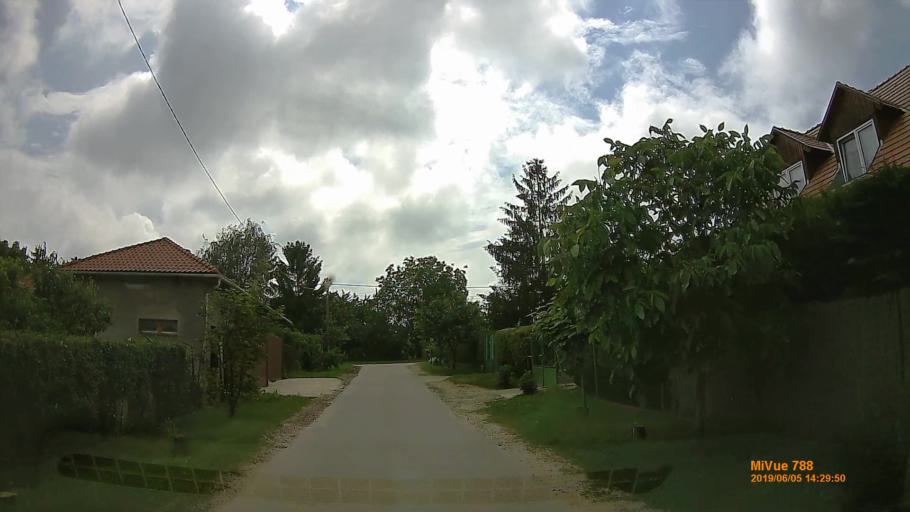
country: HU
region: Pest
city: Kistarcsa
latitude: 47.5632
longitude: 19.2594
